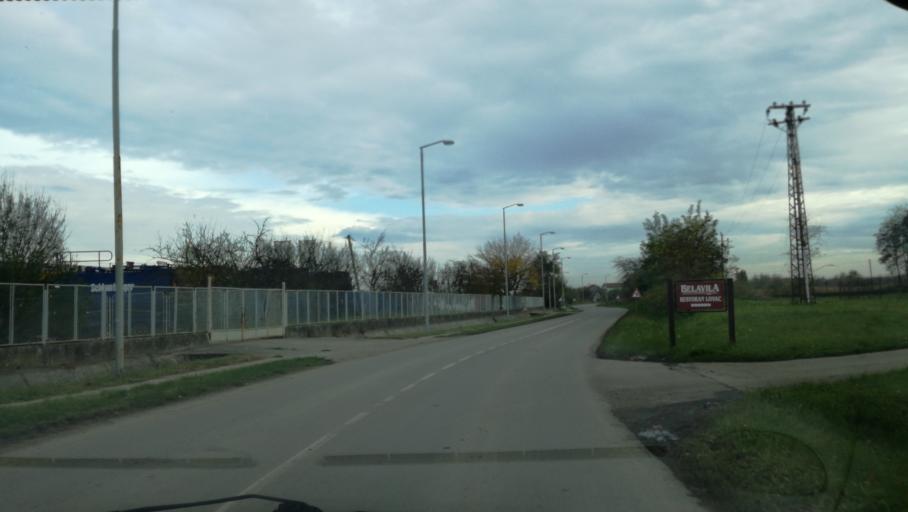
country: RS
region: Autonomna Pokrajina Vojvodina
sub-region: Severnobanatski Okrug
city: Kikinda
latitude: 45.8459
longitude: 20.4674
